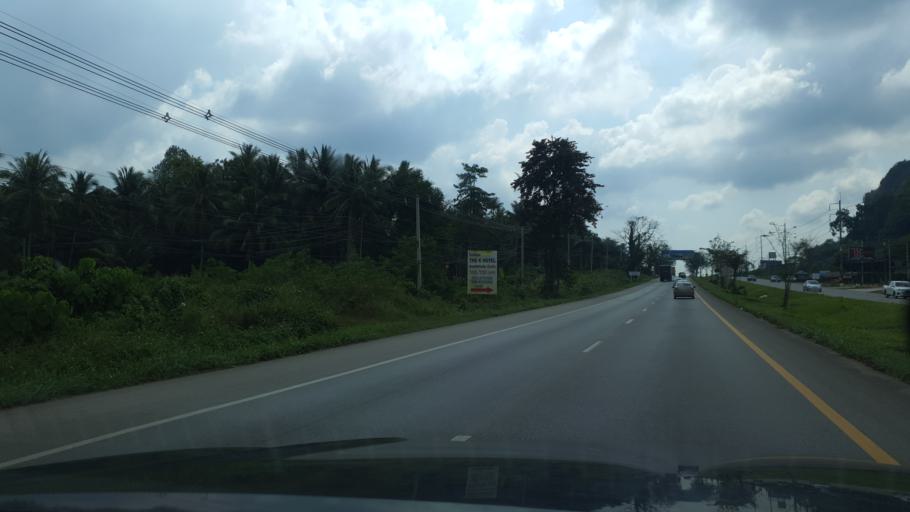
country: TH
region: Chumphon
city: Chumphon
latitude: 10.4715
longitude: 99.1282
